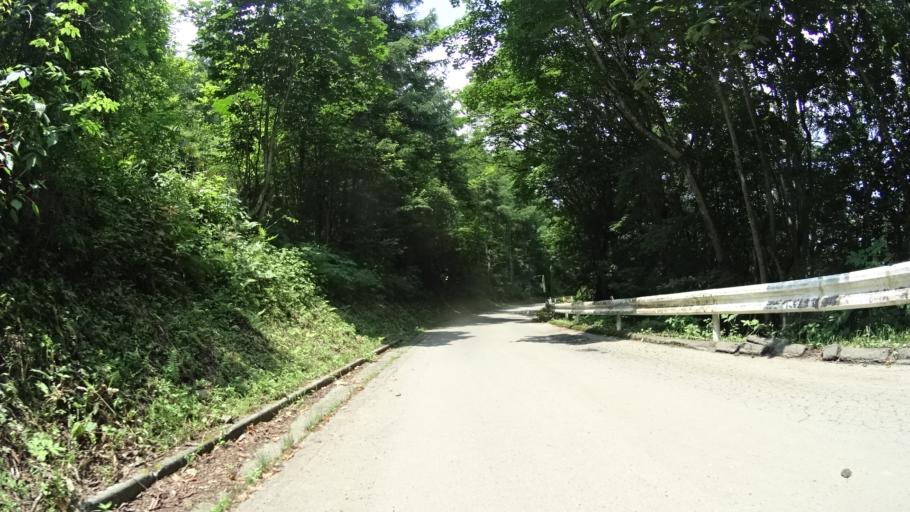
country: JP
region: Nagano
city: Saku
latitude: 36.1013
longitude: 138.6506
